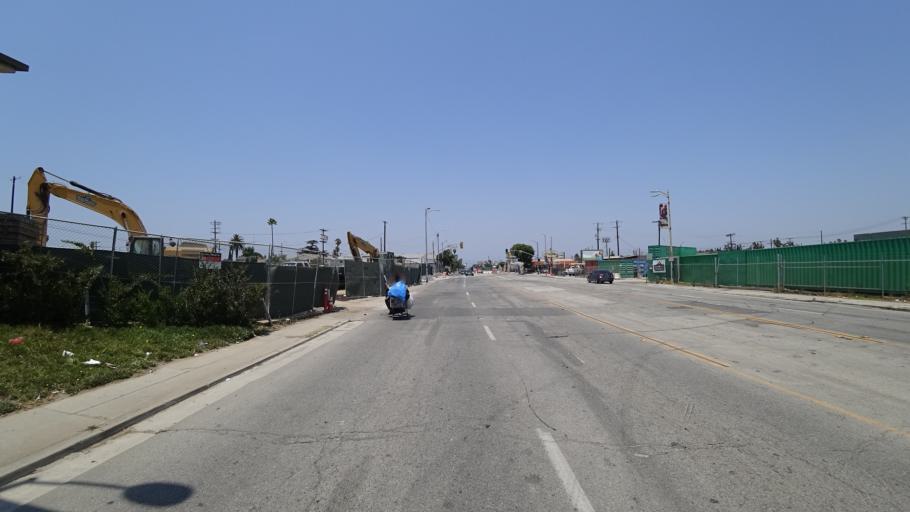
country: US
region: California
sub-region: Los Angeles County
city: View Park-Windsor Hills
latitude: 33.9774
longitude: -118.3310
